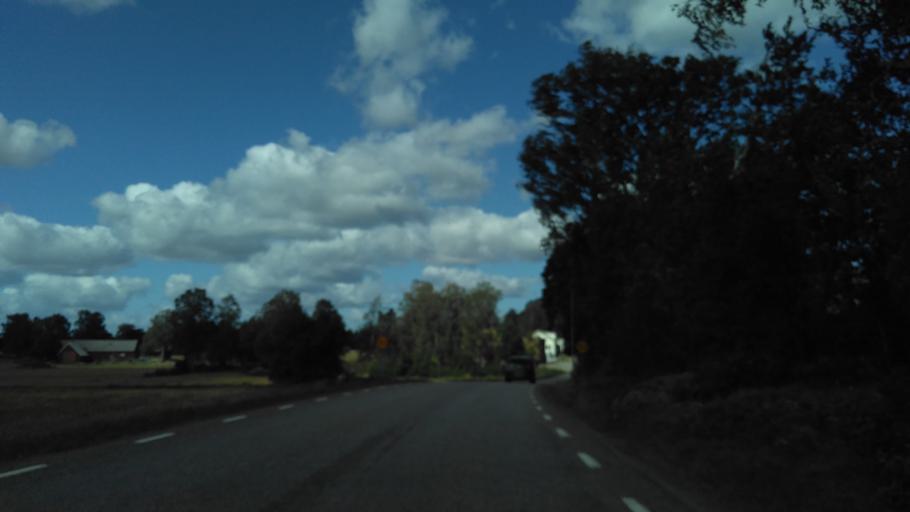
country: SE
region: Vaestra Goetaland
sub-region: Herrljunga Kommun
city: Herrljunga
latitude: 58.1410
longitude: 13.0272
